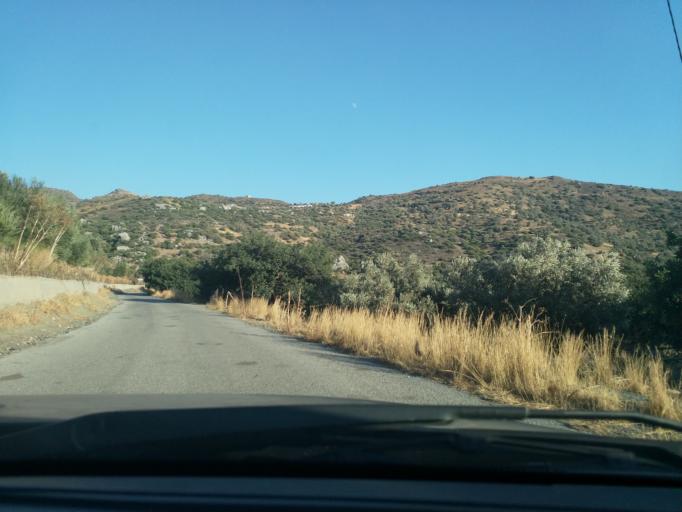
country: GR
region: Crete
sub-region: Nomos Rethymnis
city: Agia Galini
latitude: 35.1165
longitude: 24.5635
